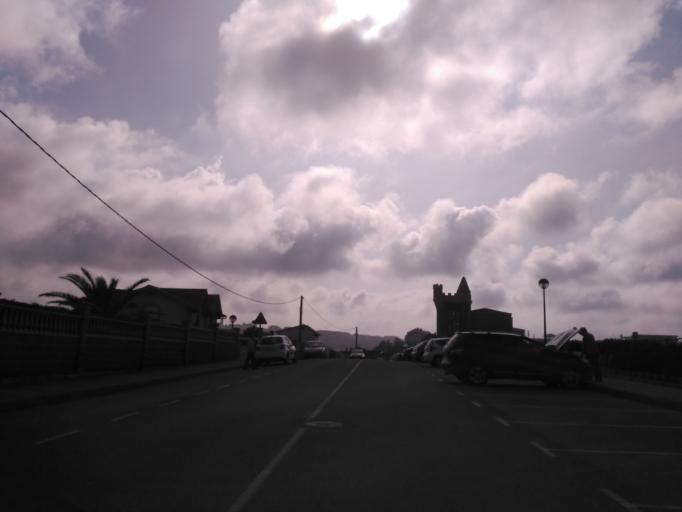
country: ES
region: Cantabria
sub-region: Provincia de Cantabria
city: Suances
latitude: 43.4395
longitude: -4.0450
